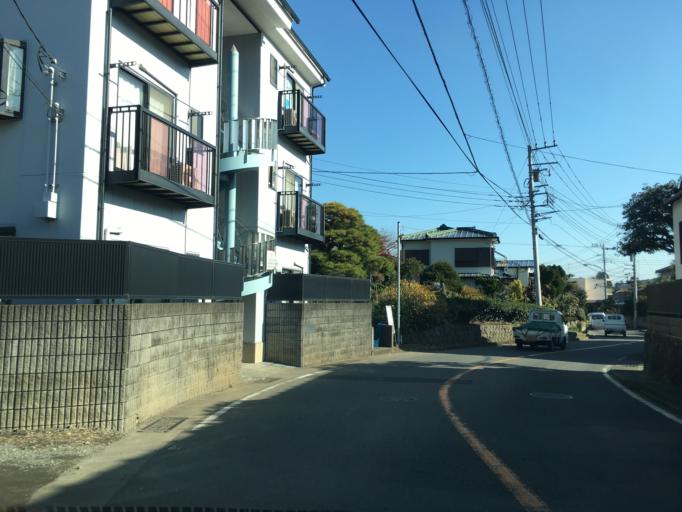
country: JP
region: Kanagawa
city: Odawara
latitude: 35.2605
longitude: 139.1419
